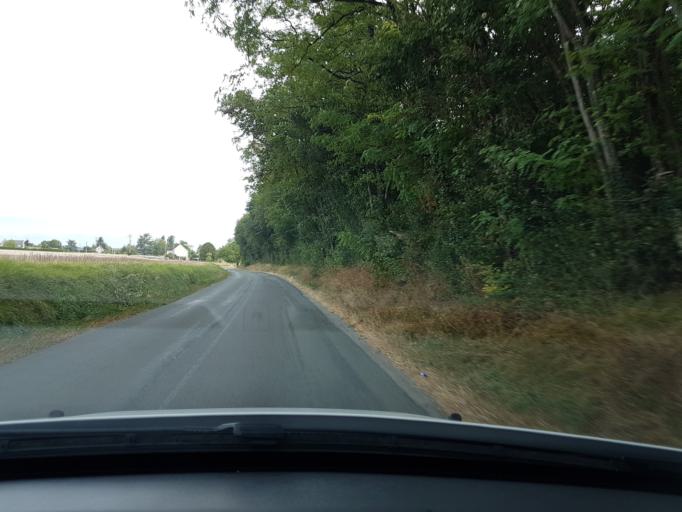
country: FR
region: Centre
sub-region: Departement d'Indre-et-Loire
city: Azay-sur-Cher
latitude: 47.3404
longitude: 0.8314
